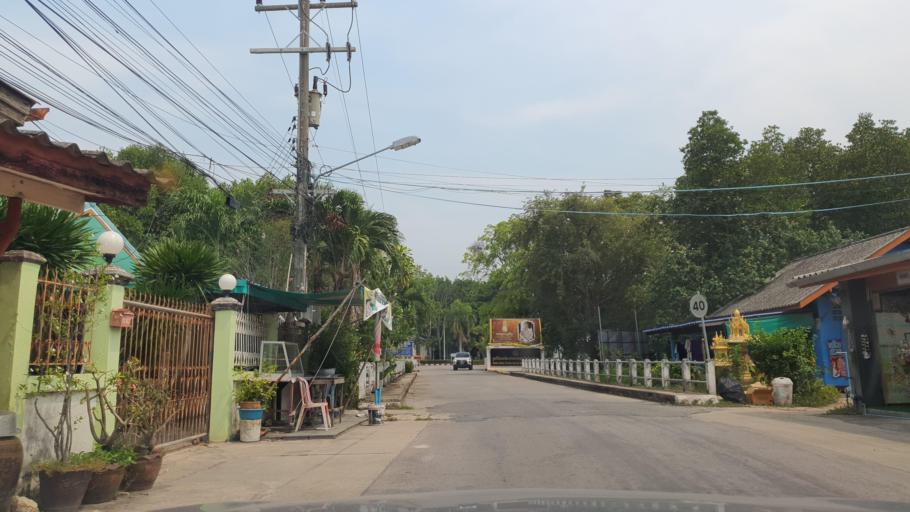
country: TH
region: Rayong
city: Rayong
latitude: 12.6112
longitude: 101.4222
